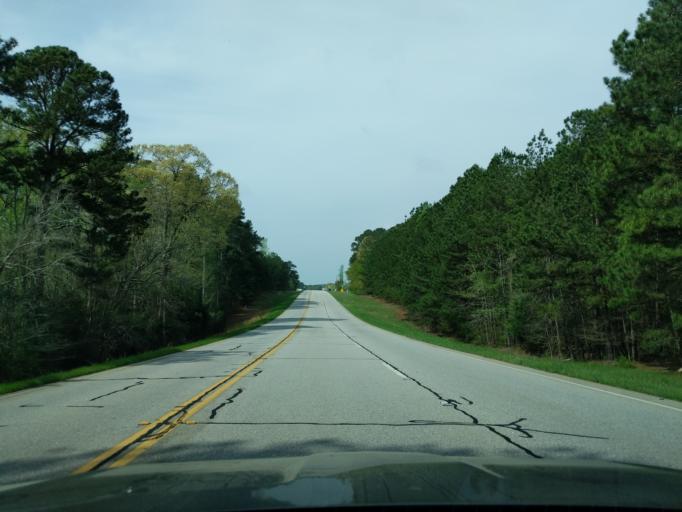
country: US
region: Georgia
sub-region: Lincoln County
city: Lincolnton
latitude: 33.8469
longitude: -82.4042
